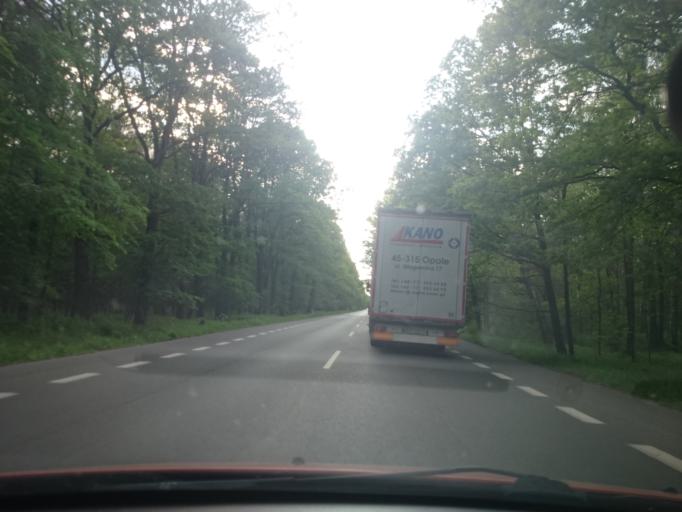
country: PL
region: Opole Voivodeship
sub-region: Powiat opolski
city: Chrzastowice
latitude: 50.6324
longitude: 18.0205
